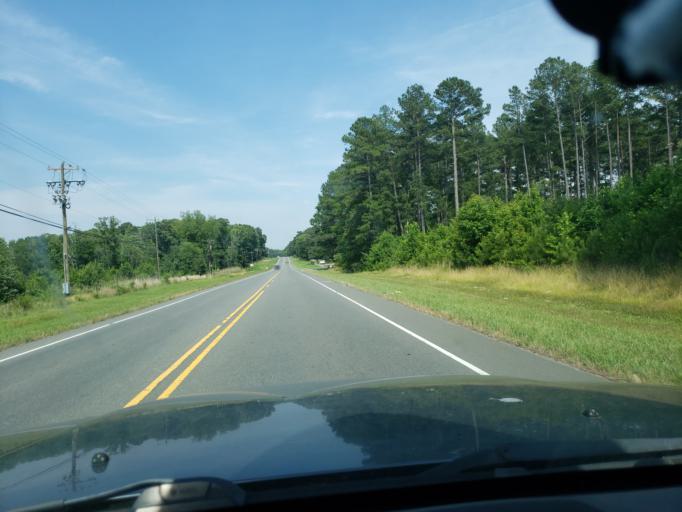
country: US
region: North Carolina
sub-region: Orange County
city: Carrboro
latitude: 35.9242
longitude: -79.1740
